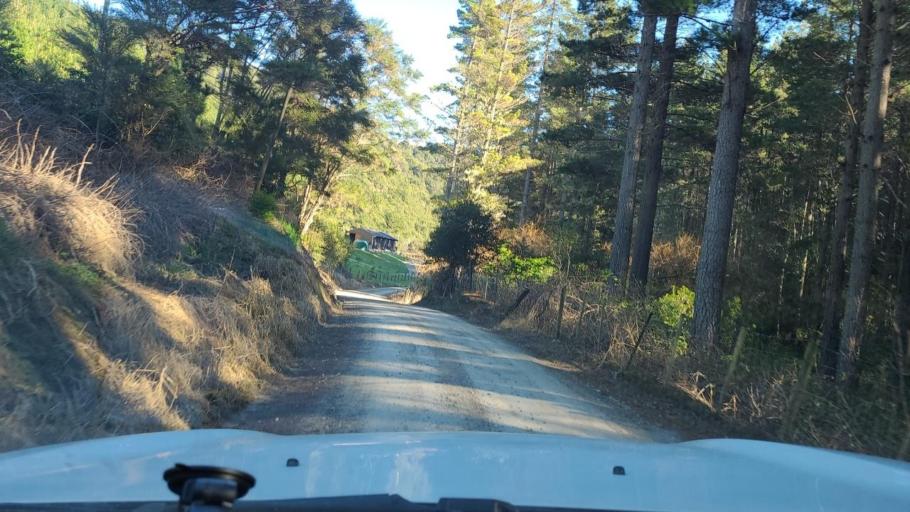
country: NZ
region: Gisborne
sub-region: Gisborne District
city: Gisborne
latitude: -38.6260
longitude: 178.0444
